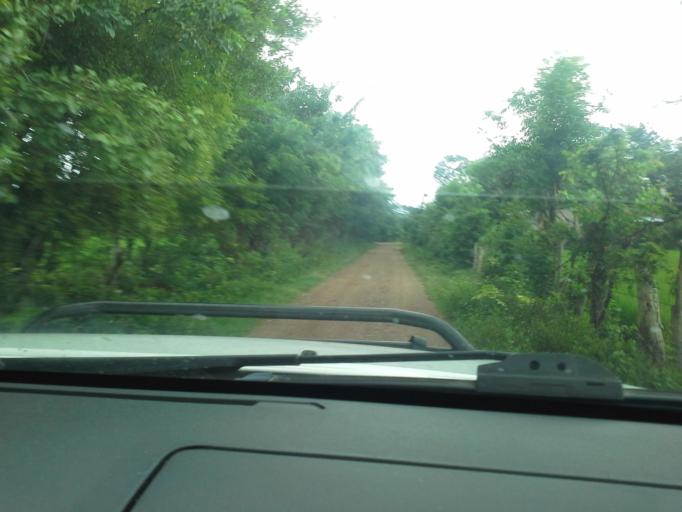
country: NI
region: Matagalpa
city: Ciudad Dario
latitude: 12.8215
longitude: -86.1930
